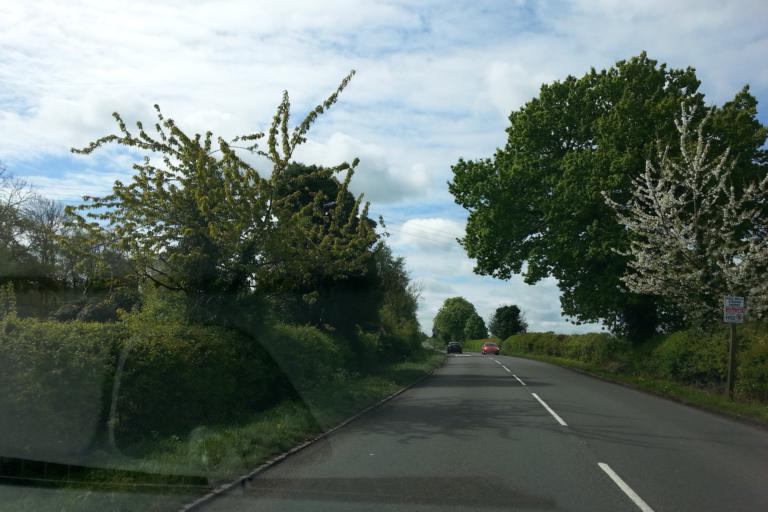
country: GB
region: England
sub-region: Staffordshire
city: Lichfield
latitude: 52.7239
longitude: -1.8385
